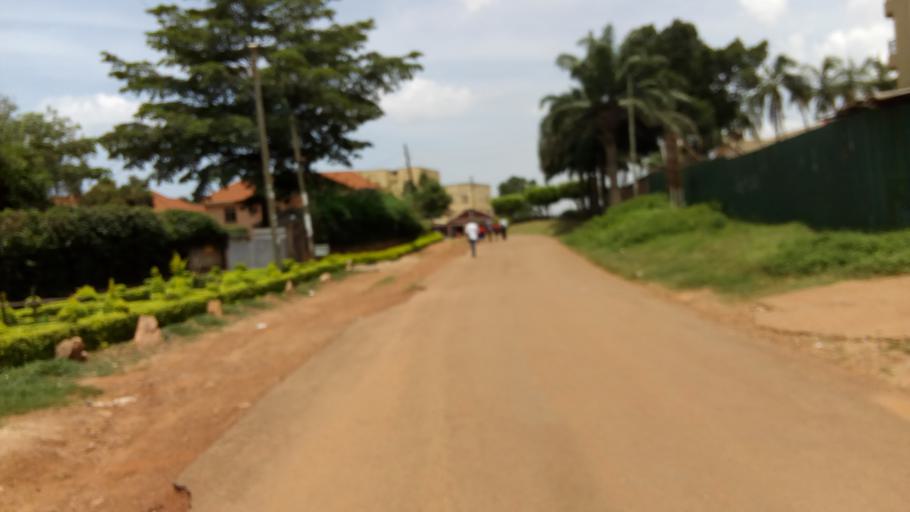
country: UG
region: Central Region
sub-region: Wakiso District
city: Kireka
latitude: 0.3250
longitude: 32.6348
